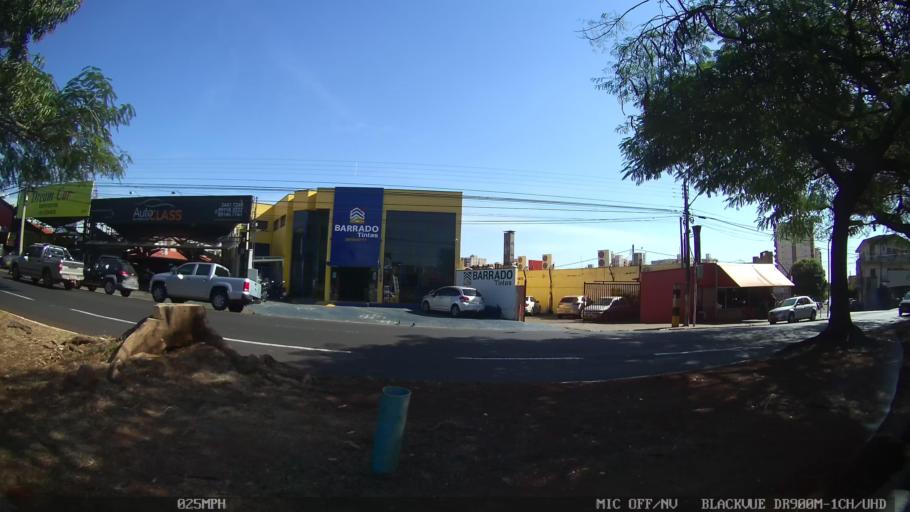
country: BR
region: Sao Paulo
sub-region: Ribeirao Preto
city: Ribeirao Preto
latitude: -21.1817
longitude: -47.7863
